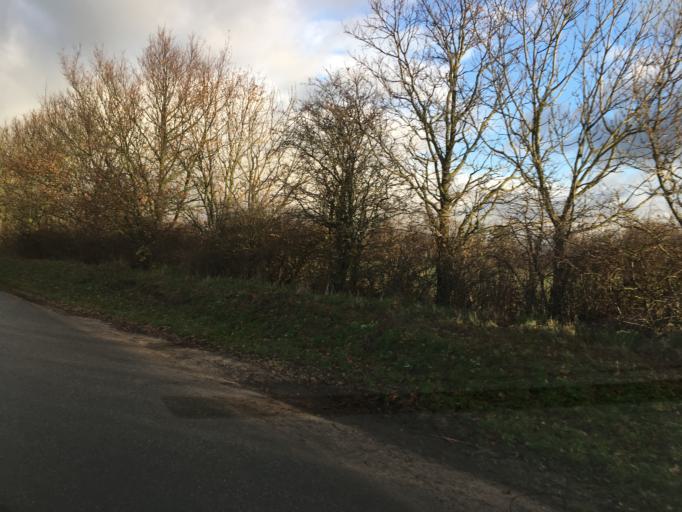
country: DK
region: South Denmark
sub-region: Tonder Kommune
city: Sherrebek
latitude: 55.1487
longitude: 8.7936
